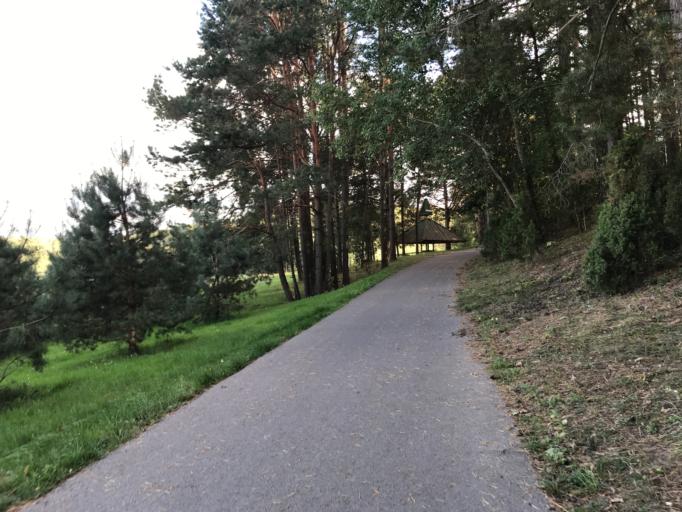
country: LT
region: Alytaus apskritis
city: Druskininkai
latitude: 54.0166
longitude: 23.9601
